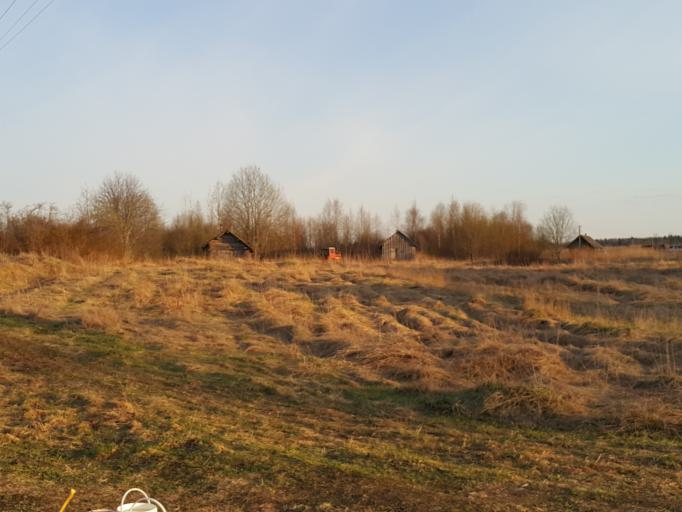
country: RU
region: Leningrad
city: Podporozh'ye
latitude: 60.3531
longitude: 34.8373
